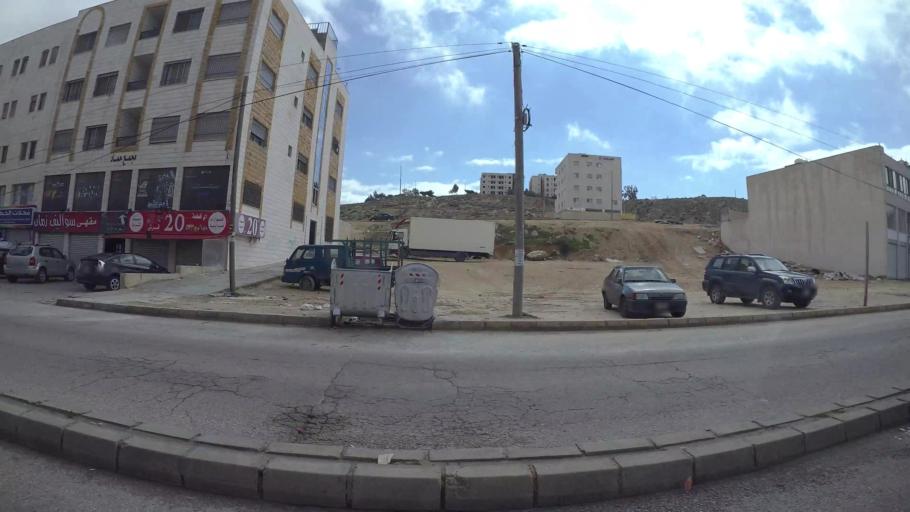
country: JO
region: Amman
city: Al Jubayhah
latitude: 32.0625
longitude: 35.8807
